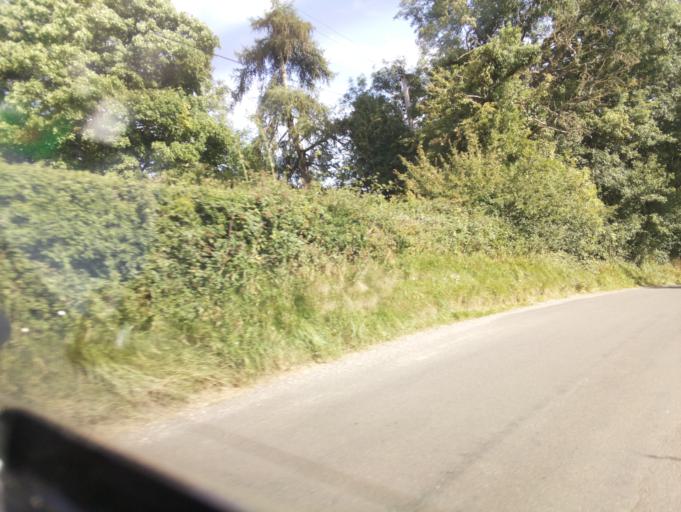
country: GB
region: England
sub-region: Gloucestershire
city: Tetbury
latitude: 51.6596
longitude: -2.1441
